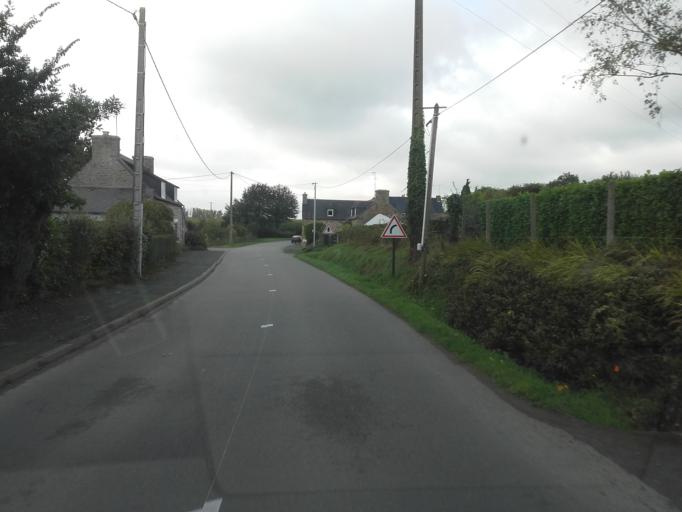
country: FR
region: Brittany
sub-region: Departement des Cotes-d'Armor
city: Plelo
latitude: 48.5682
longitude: -2.9504
